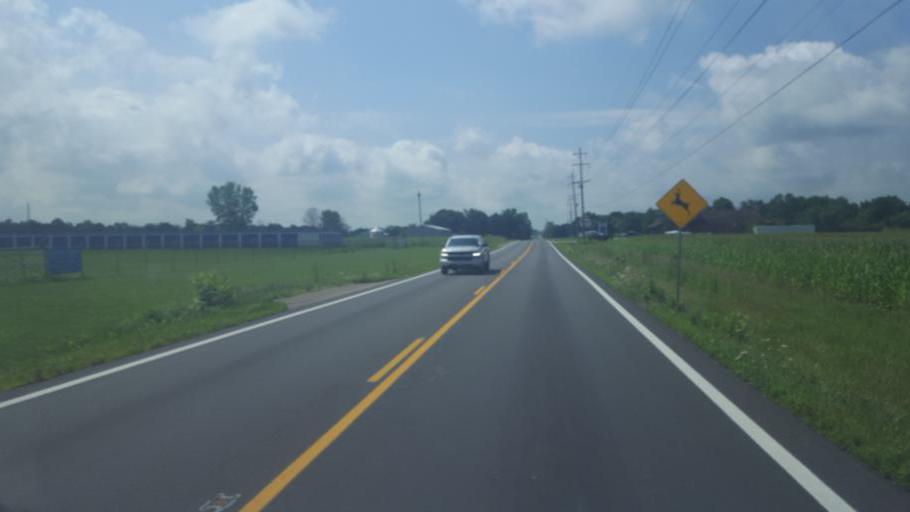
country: US
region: Ohio
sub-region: Fairfield County
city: Baltimore
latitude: 39.8305
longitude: -82.5693
